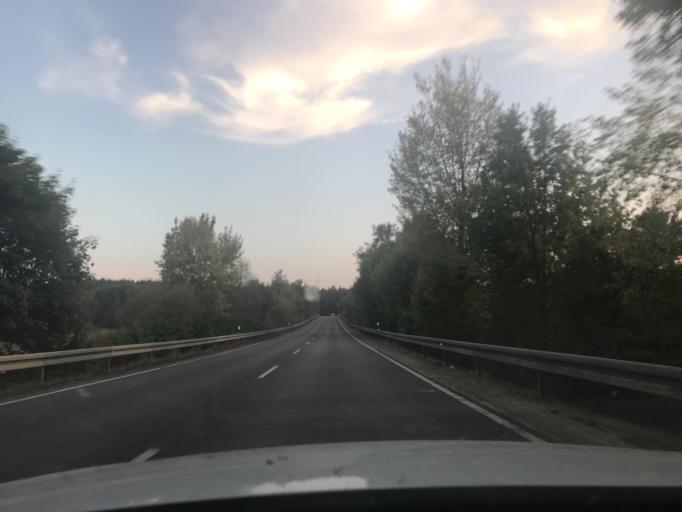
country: DE
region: Bavaria
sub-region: Upper Franconia
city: Emtmannsberg
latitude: 49.8885
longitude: 11.6121
